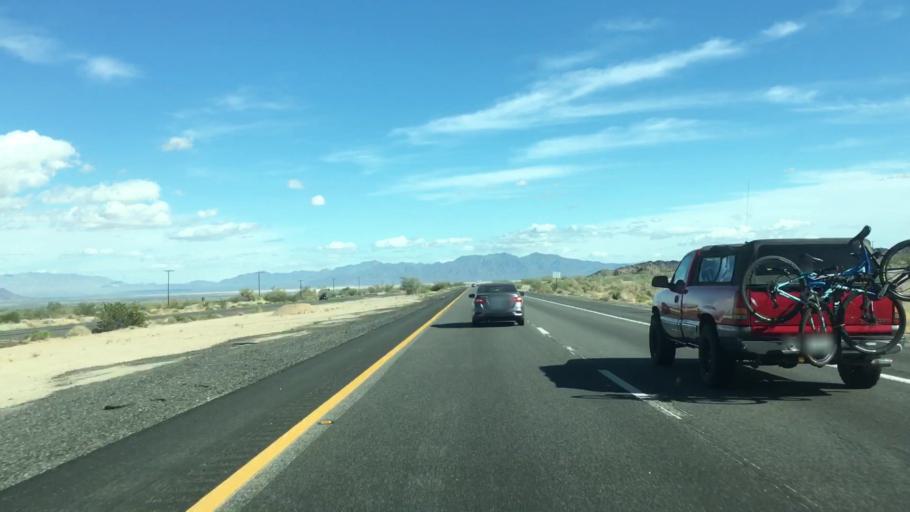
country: US
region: California
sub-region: Imperial County
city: Niland
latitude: 33.7032
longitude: -115.4471
